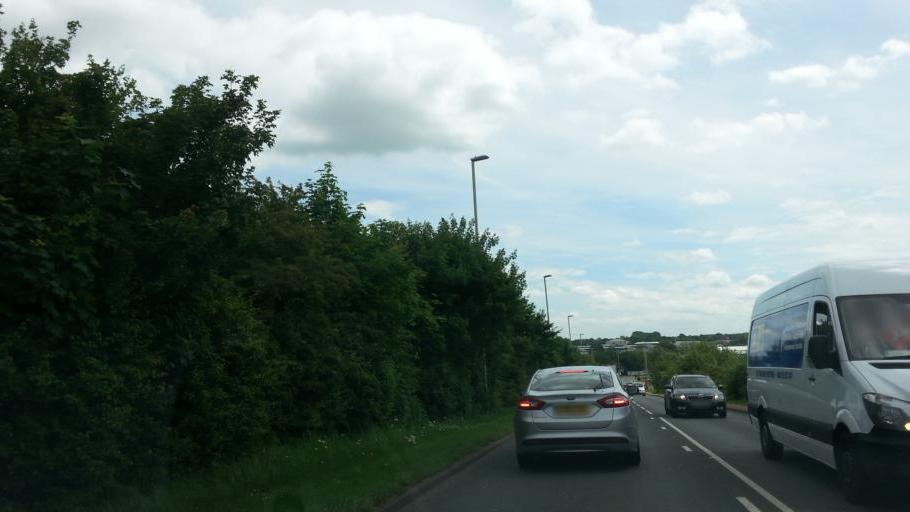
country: GB
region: England
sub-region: Leicestershire
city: Syston
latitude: 52.6634
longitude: -1.0929
